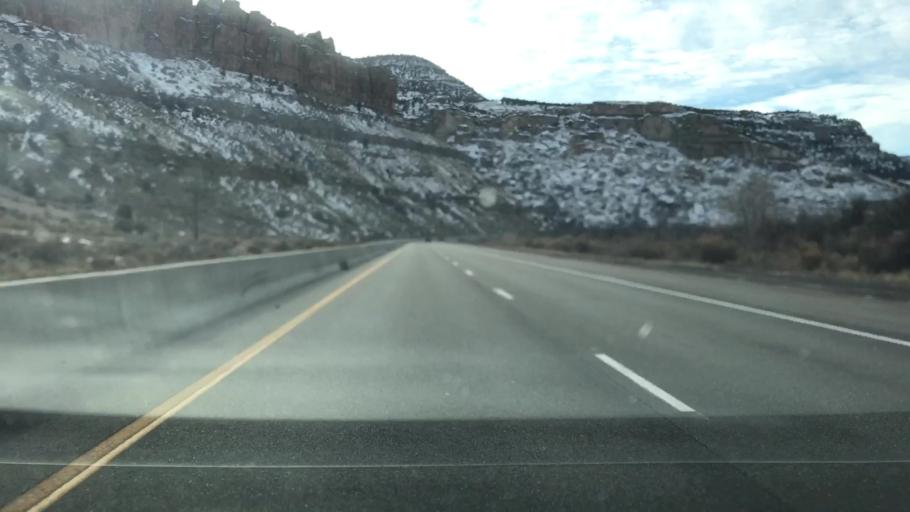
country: US
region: Colorado
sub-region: Mesa County
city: Palisade
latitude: 39.2143
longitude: -108.2564
